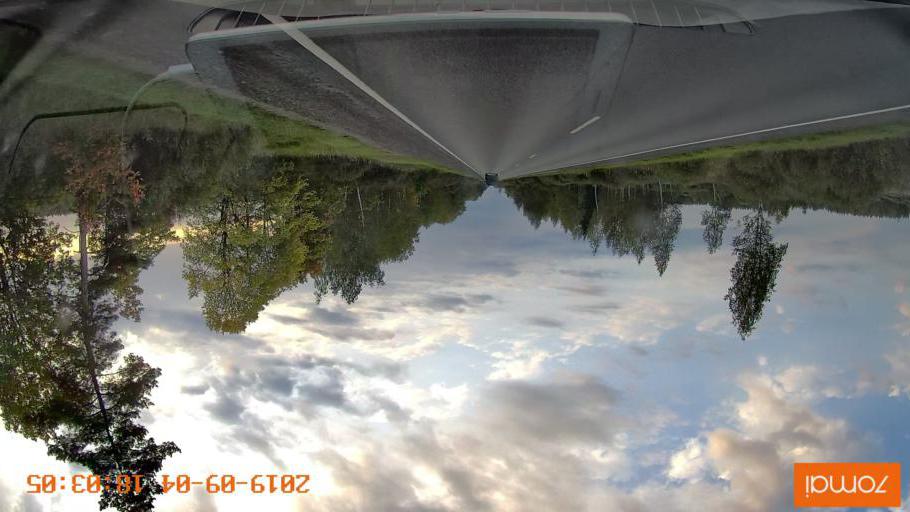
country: RU
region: Moskovskaya
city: Il'inskiy Pogost
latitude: 55.4675
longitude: 38.8569
